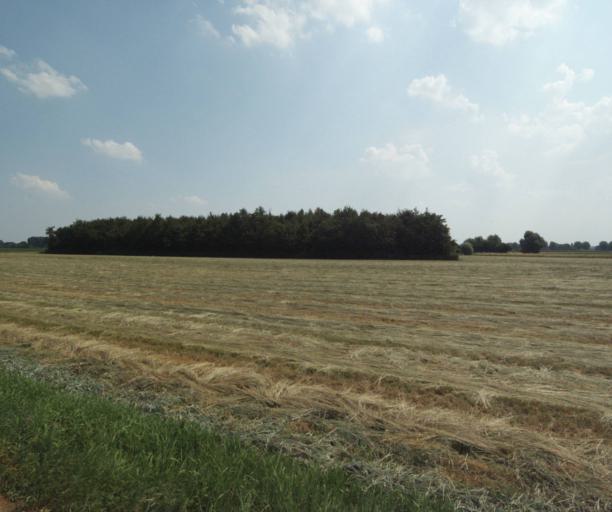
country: FR
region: Nord-Pas-de-Calais
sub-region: Departement du Nord
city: Comines
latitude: 50.7319
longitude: 3.0365
